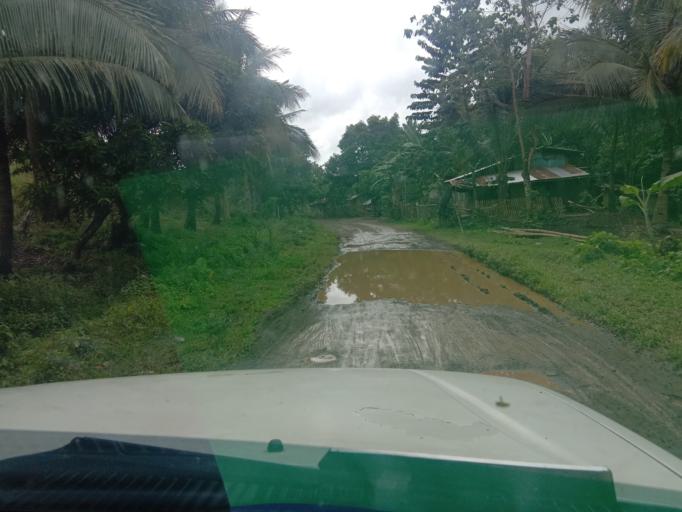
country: PH
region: Western Visayas
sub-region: Province of Capiz
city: Lantangan
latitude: 11.3721
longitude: 122.8920
